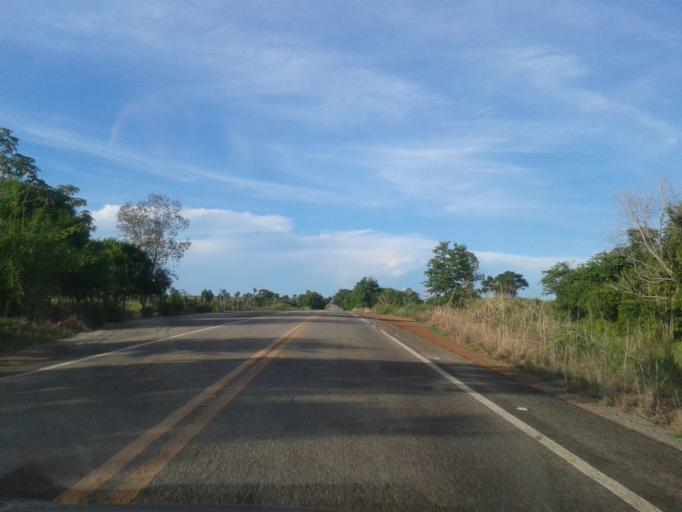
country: BR
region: Goias
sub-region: Sao Miguel Do Araguaia
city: Sao Miguel do Araguaia
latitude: -13.5430
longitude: -50.3076
